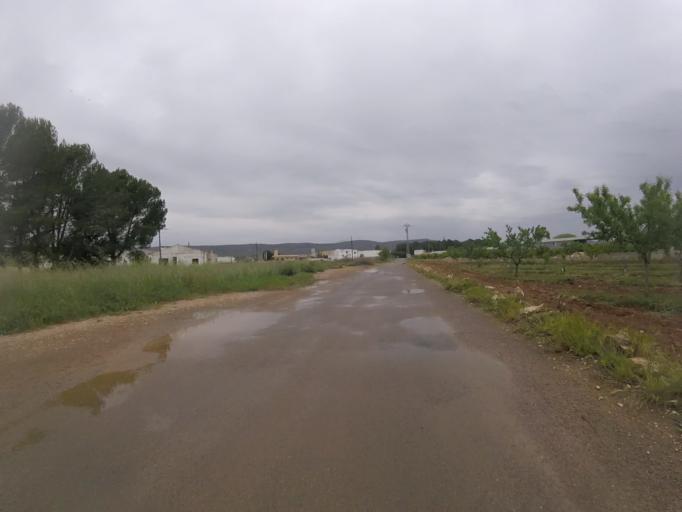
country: ES
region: Valencia
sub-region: Provincia de Castello
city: Alcala de Xivert
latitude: 40.2959
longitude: 0.2280
